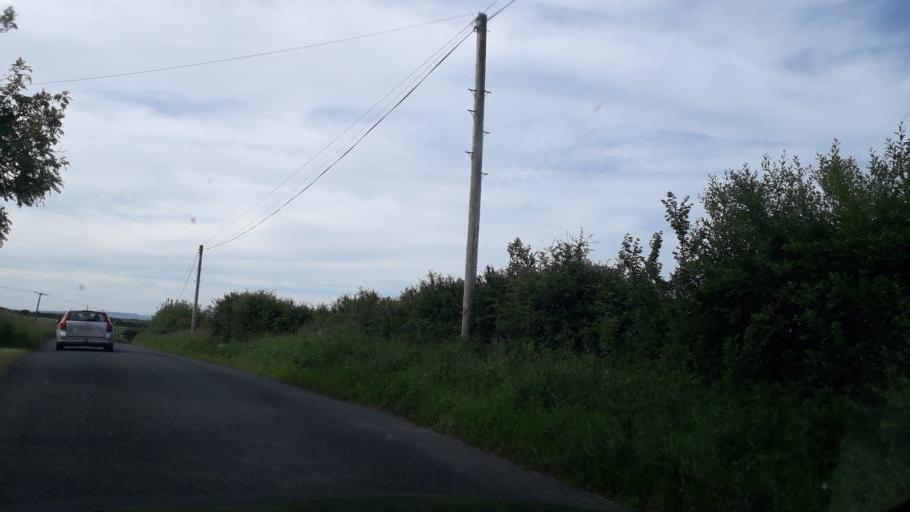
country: IE
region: Leinster
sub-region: Loch Garman
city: Courtown
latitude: 52.5361
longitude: -6.2556
